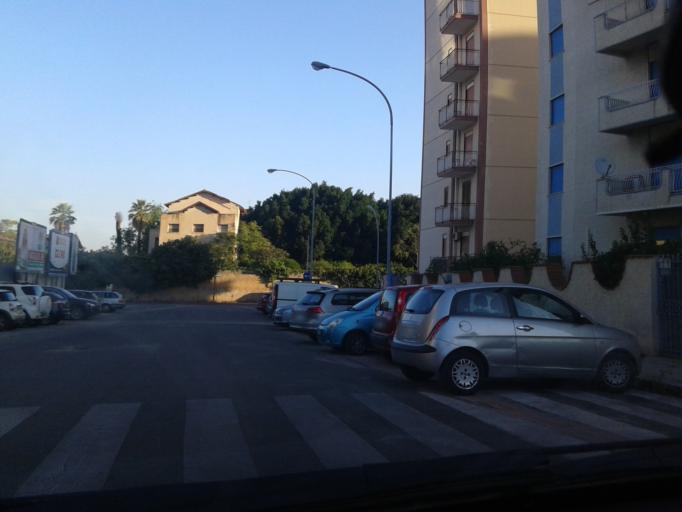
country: IT
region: Sicily
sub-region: Palermo
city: Palermo
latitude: 38.1071
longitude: 13.3351
